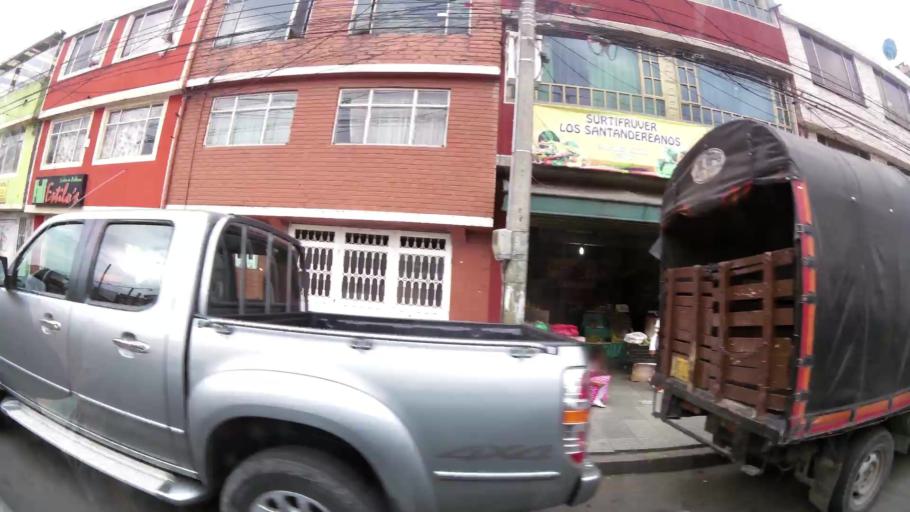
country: CO
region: Bogota D.C.
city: Bogota
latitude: 4.6050
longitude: -74.1360
